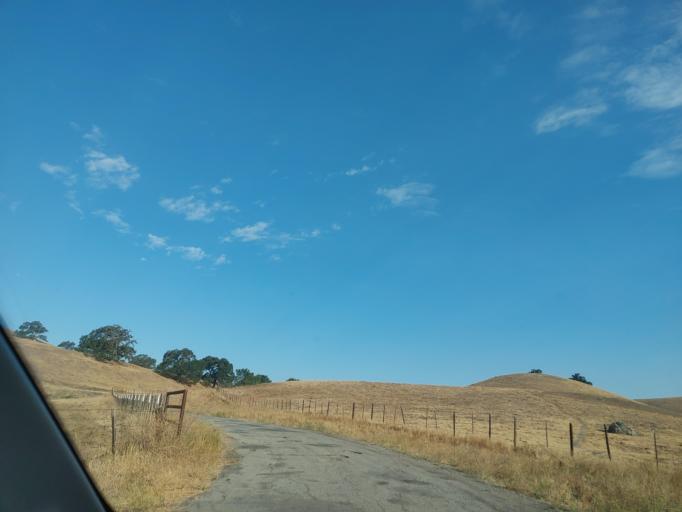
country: US
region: California
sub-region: San Benito County
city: Ridgemark
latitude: 36.7582
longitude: -121.1689
